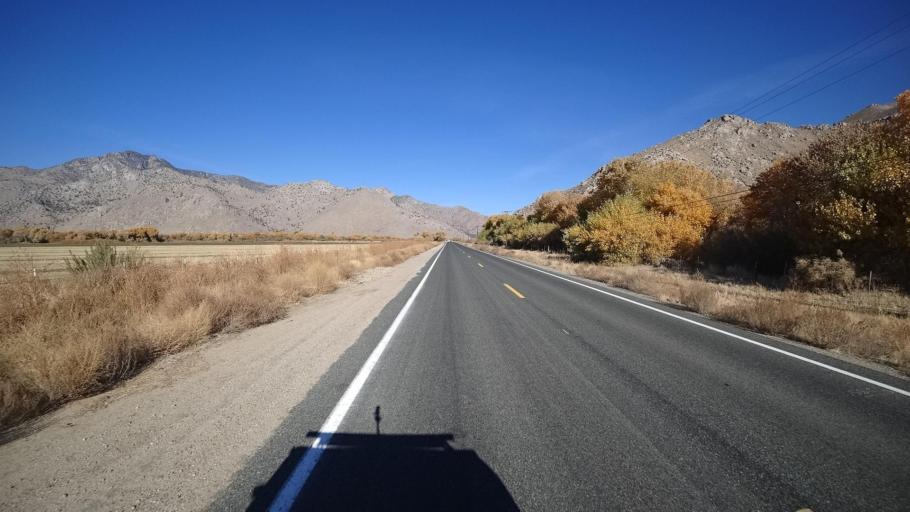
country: US
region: California
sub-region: Kern County
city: Weldon
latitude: 35.6750
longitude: -118.2566
